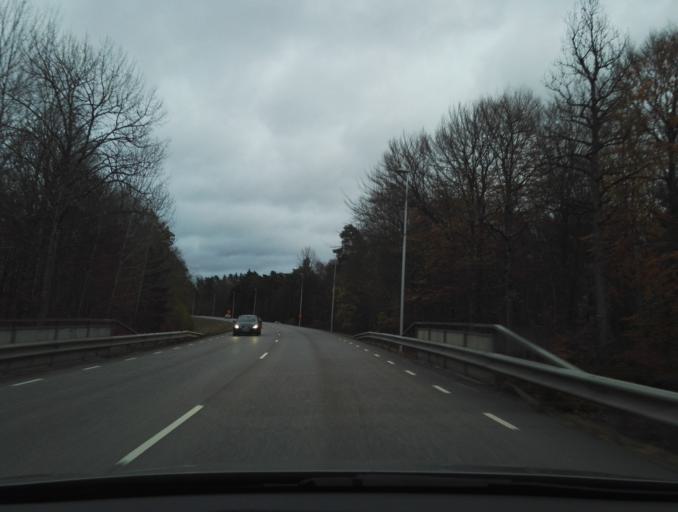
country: SE
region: Kronoberg
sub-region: Vaxjo Kommun
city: Vaexjoe
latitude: 56.8651
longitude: 14.7917
